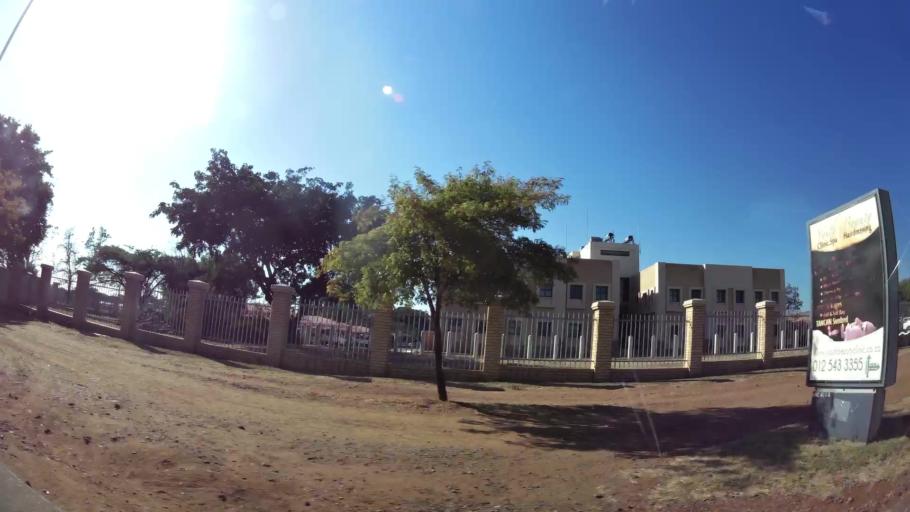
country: ZA
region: Gauteng
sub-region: City of Tshwane Metropolitan Municipality
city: Pretoria
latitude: -25.6745
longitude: 28.2432
